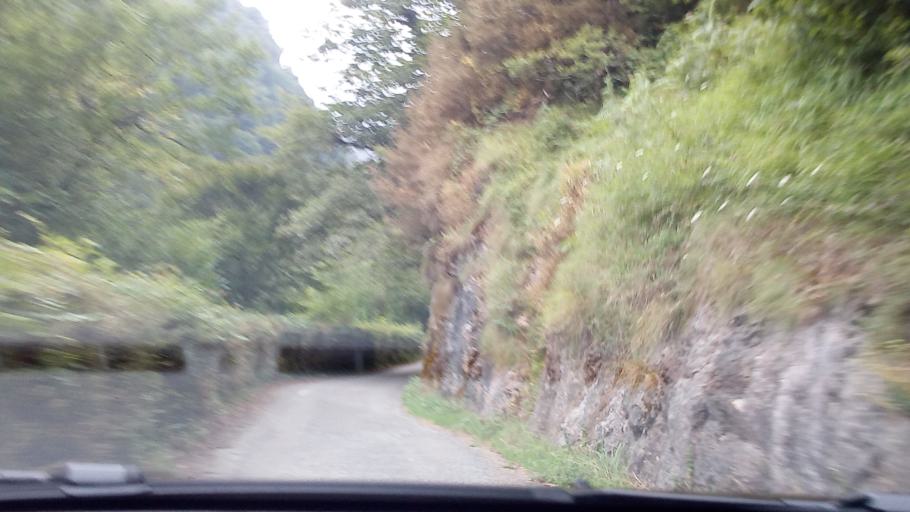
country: FR
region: Aquitaine
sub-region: Departement des Pyrenees-Atlantiques
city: Laruns
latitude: 42.9770
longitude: -0.4285
